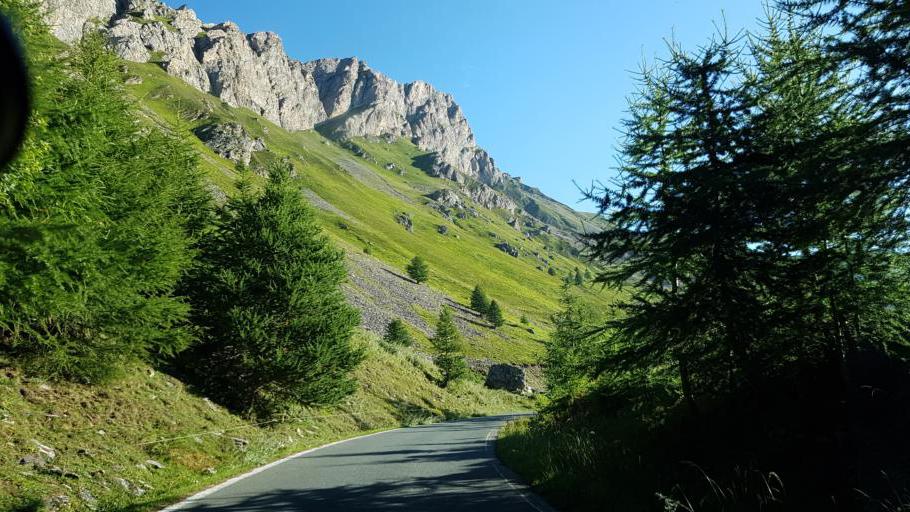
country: IT
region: Piedmont
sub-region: Provincia di Cuneo
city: Pontechianale
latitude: 44.6607
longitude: 6.9913
